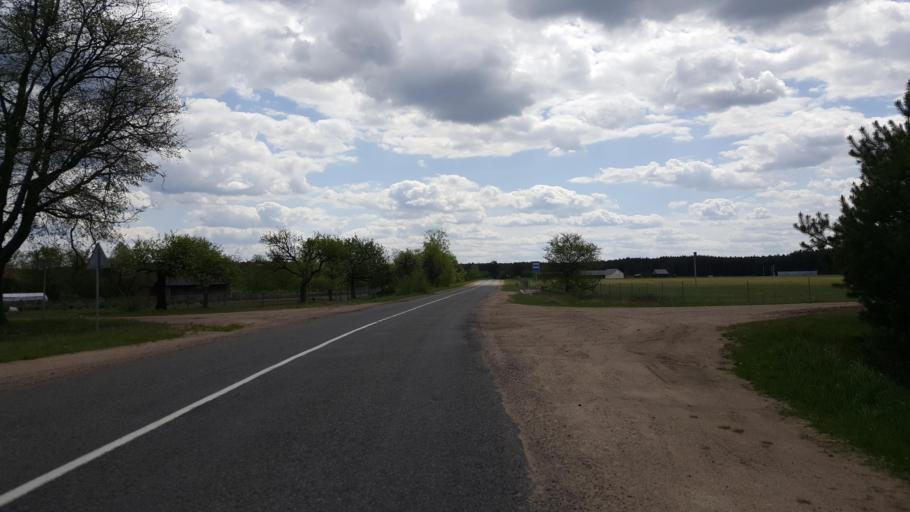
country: BY
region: Brest
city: Zhabinka
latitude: 52.3940
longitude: 24.0949
